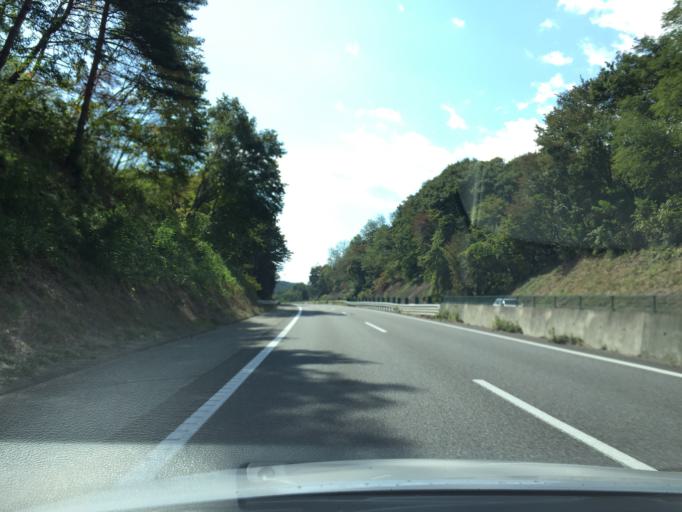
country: JP
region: Fukushima
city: Sukagawa
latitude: 37.2187
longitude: 140.3112
